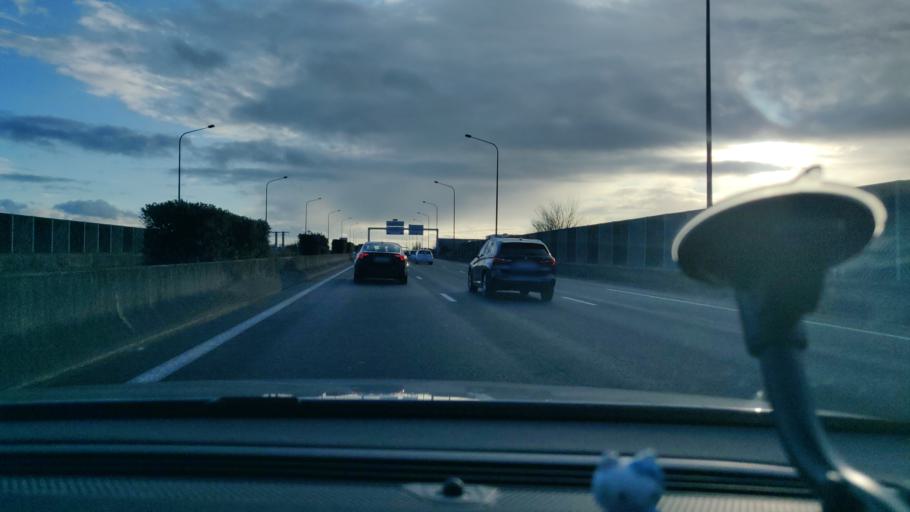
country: FR
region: Midi-Pyrenees
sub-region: Departement de la Haute-Garonne
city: Colomiers
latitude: 43.6043
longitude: 1.3672
